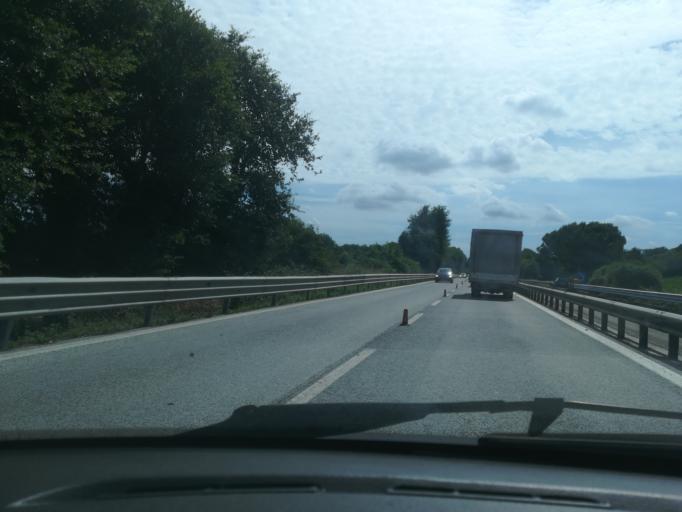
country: IT
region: The Marches
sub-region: Provincia di Macerata
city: Zona Industriale
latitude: 43.2692
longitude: 13.5083
